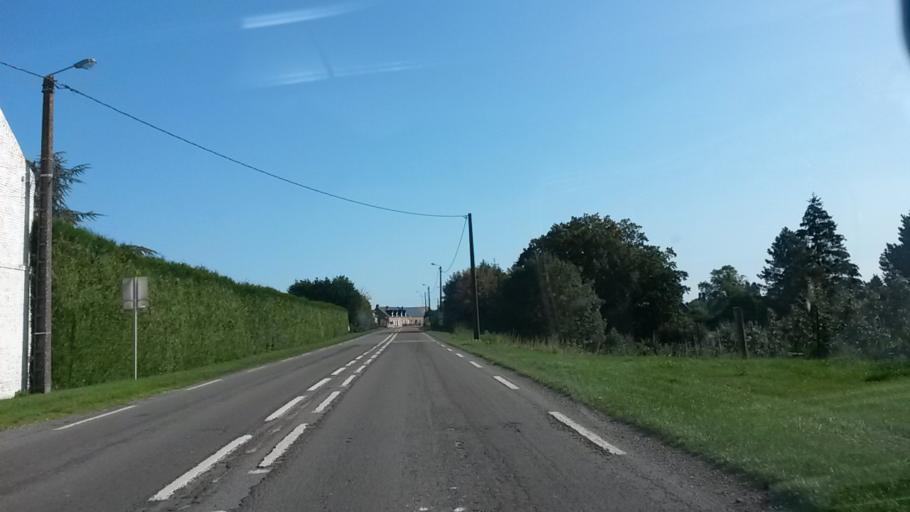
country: FR
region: Picardie
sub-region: Departement de l'Aisne
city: Guise
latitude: 49.9205
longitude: 3.6730
